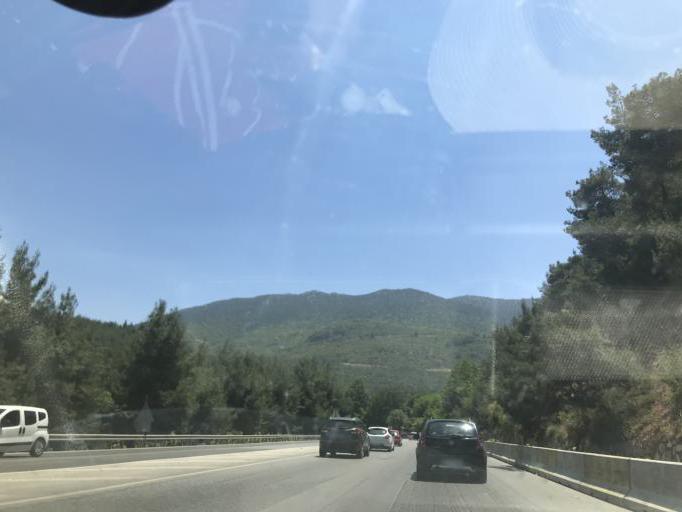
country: TR
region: Denizli
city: Denizli
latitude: 37.7297
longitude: 29.1653
